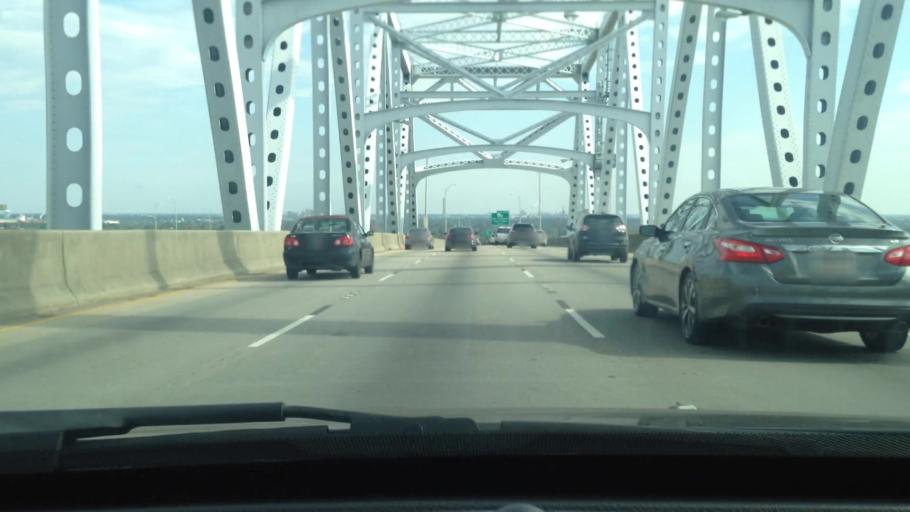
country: US
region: Louisiana
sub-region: Jefferson Parish
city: Gretna
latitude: 29.9378
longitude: -90.0535
